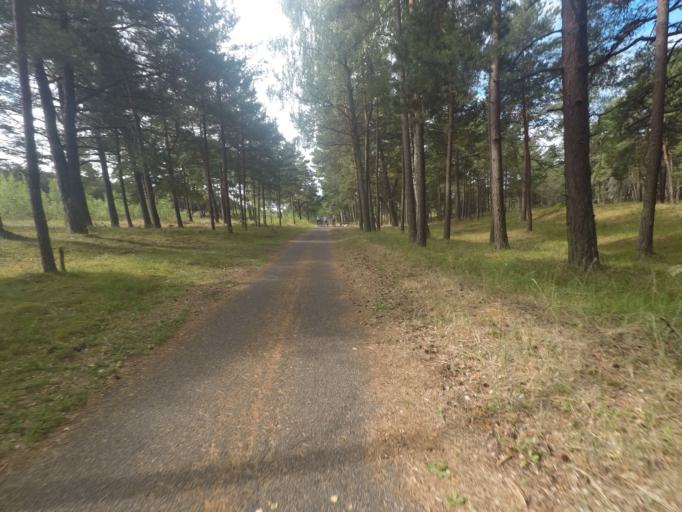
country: LT
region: Klaipedos apskritis
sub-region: Klaipeda
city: Klaipeda
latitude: 55.6120
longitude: 21.1200
